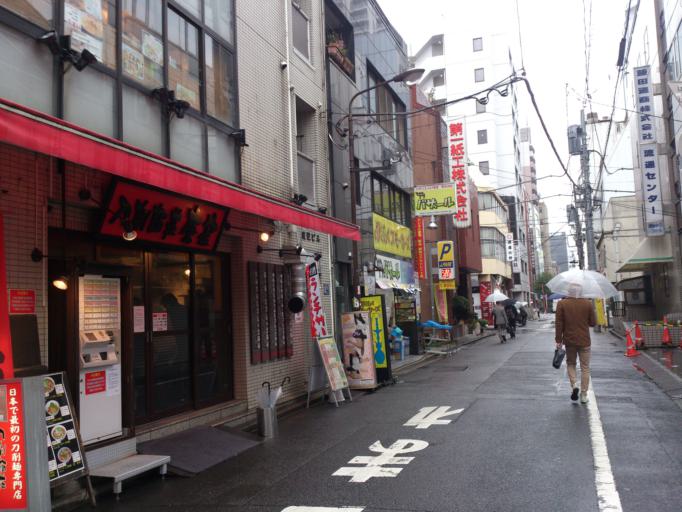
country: JP
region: Tokyo
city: Tokyo
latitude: 35.7020
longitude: 139.7706
